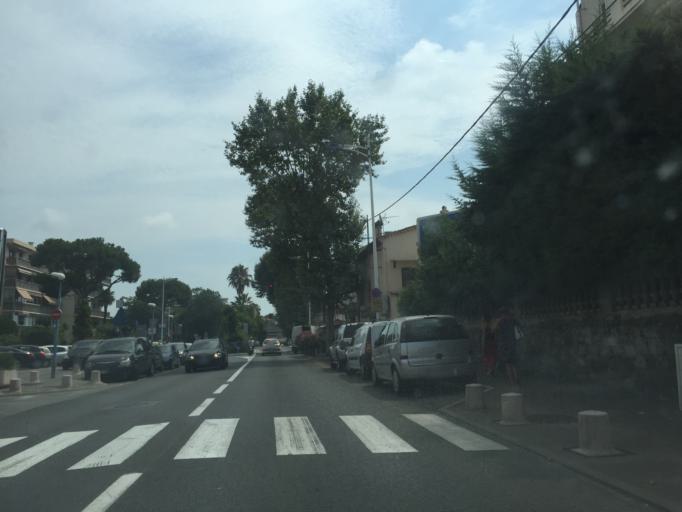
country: FR
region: Provence-Alpes-Cote d'Azur
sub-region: Departement des Alpes-Maritimes
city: Saint-Laurent-du-Var
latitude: 43.6604
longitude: 7.1755
